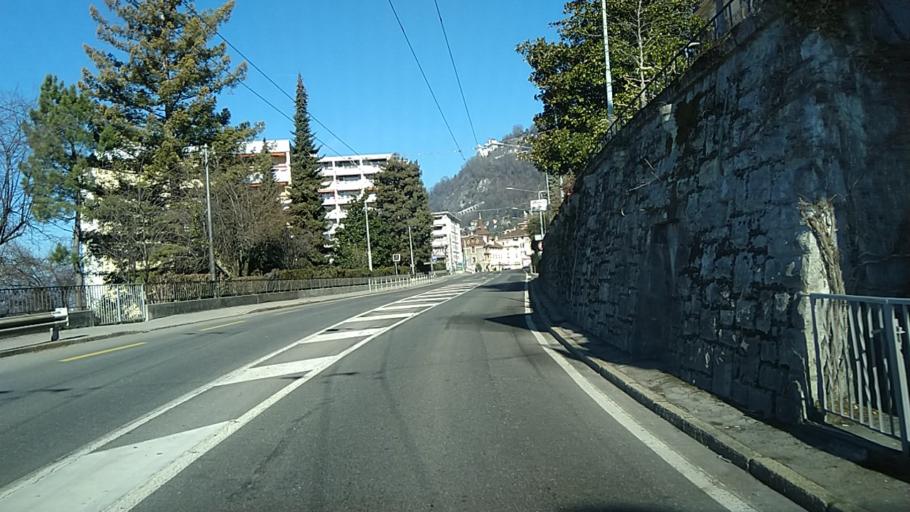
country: CH
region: Vaud
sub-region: Riviera-Pays-d'Enhaut District
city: Caux
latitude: 46.4202
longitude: 6.9261
